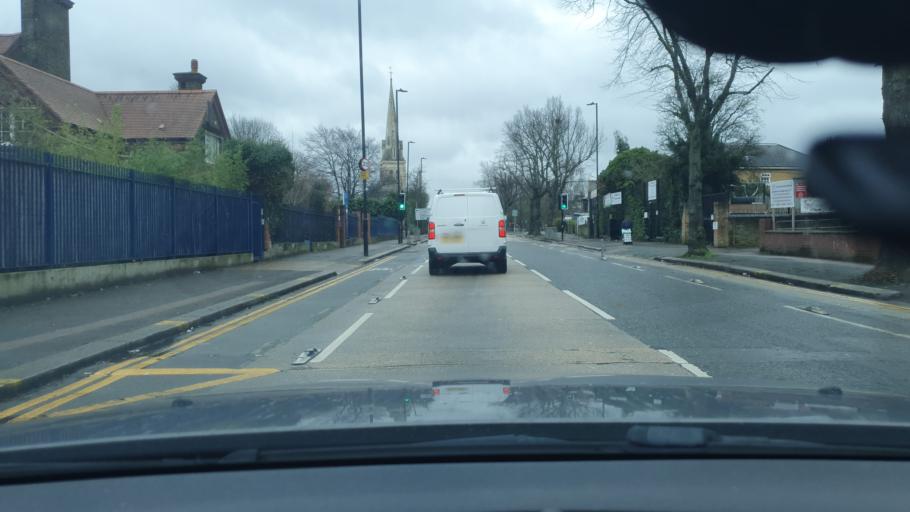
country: GB
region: England
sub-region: Greater London
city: Wood Green
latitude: 51.6000
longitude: -0.1138
